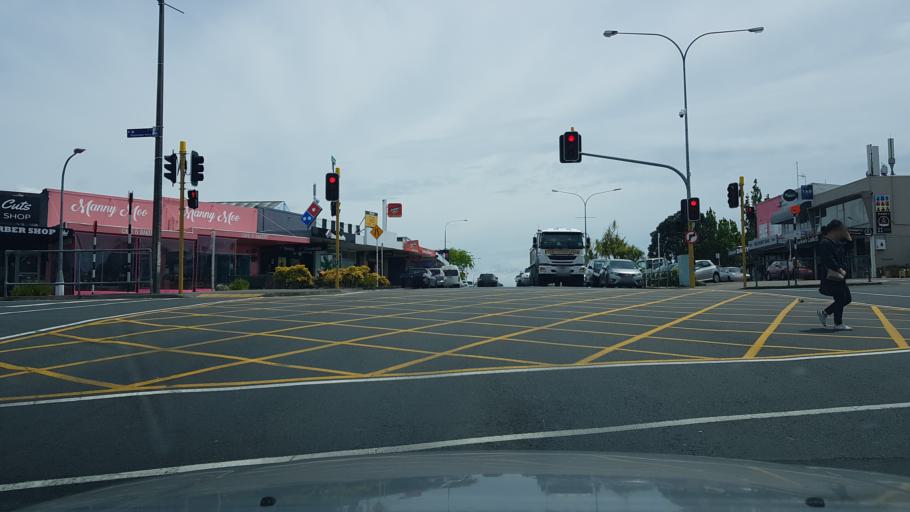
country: NZ
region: Auckland
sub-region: Auckland
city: North Shore
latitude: -36.8084
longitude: 174.7902
